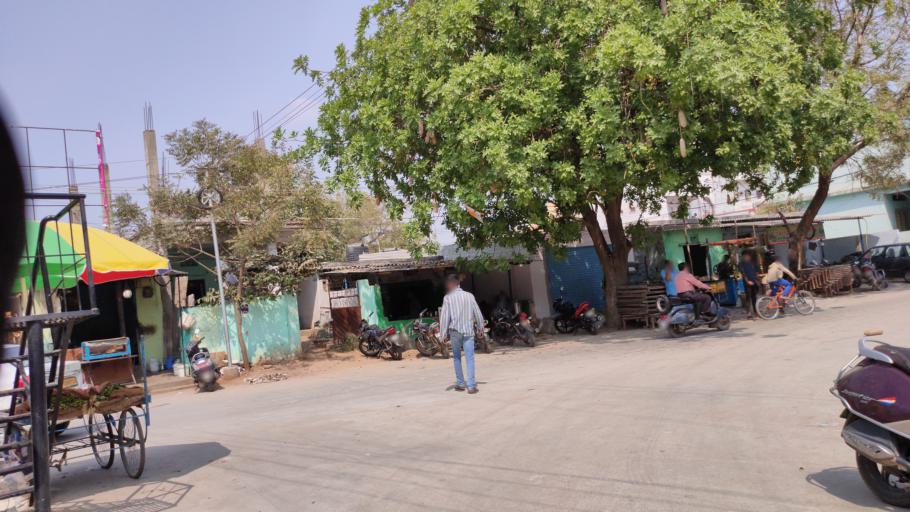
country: IN
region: Telangana
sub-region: Rangareddi
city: Quthbullapur
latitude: 17.4930
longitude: 78.4596
